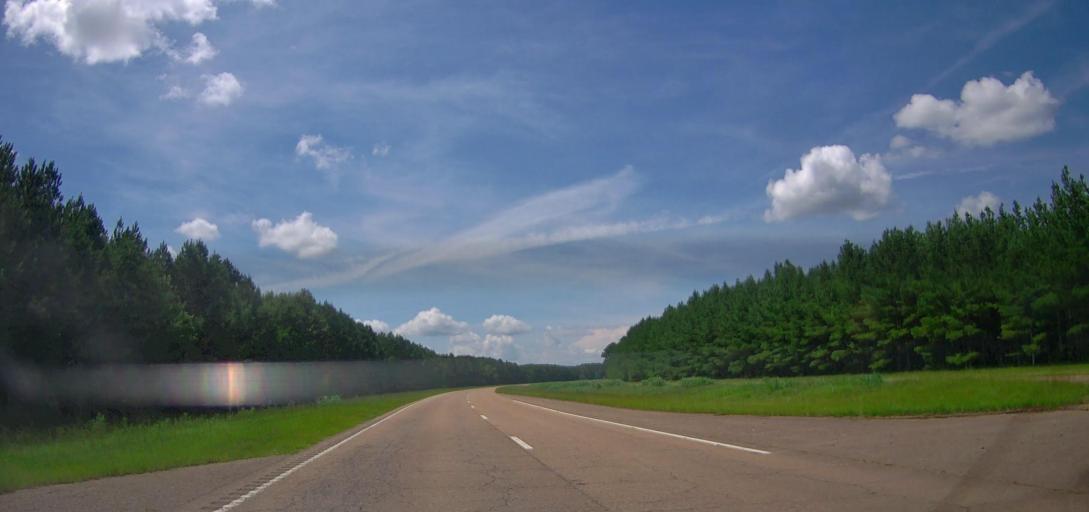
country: US
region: Mississippi
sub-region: Monroe County
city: Aberdeen
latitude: 33.8186
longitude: -88.5805
